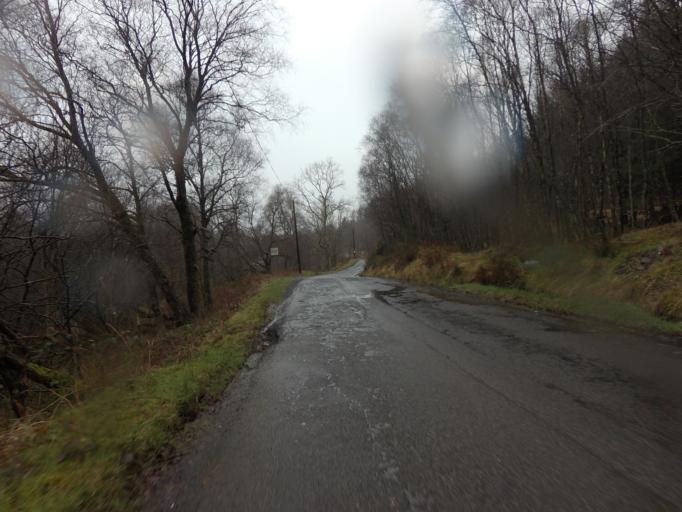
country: GB
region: Scotland
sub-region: West Dunbartonshire
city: Balloch
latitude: 56.1980
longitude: -4.5230
